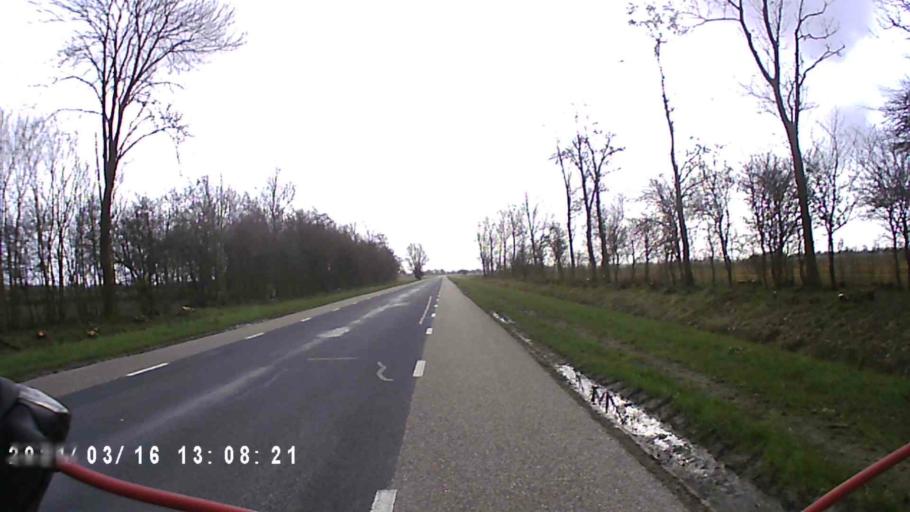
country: NL
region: Friesland
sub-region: Menameradiel
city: Berltsum
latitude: 53.2490
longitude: 5.6233
